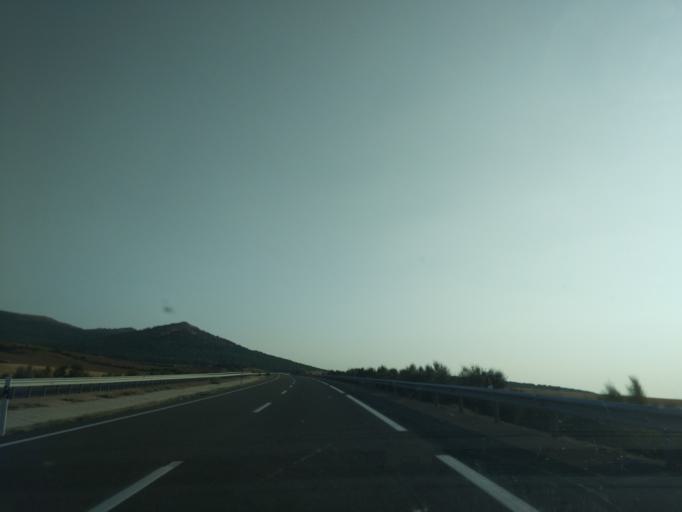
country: ES
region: Castille and Leon
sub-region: Provincia de Avila
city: Ojos-Albos
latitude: 40.7439
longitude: -4.4888
